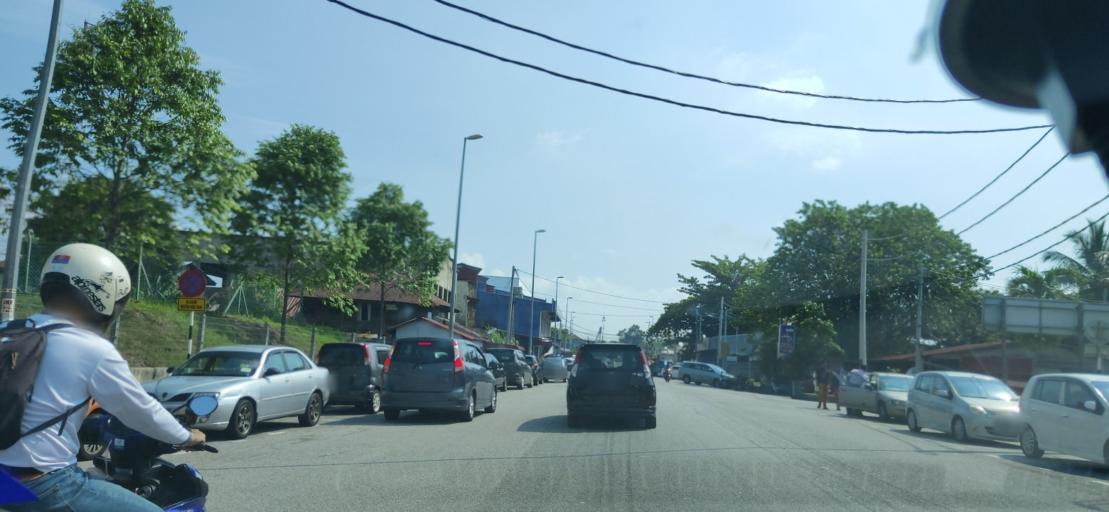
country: MY
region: Kedah
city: Sungai Petani
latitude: 5.6434
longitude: 100.4907
